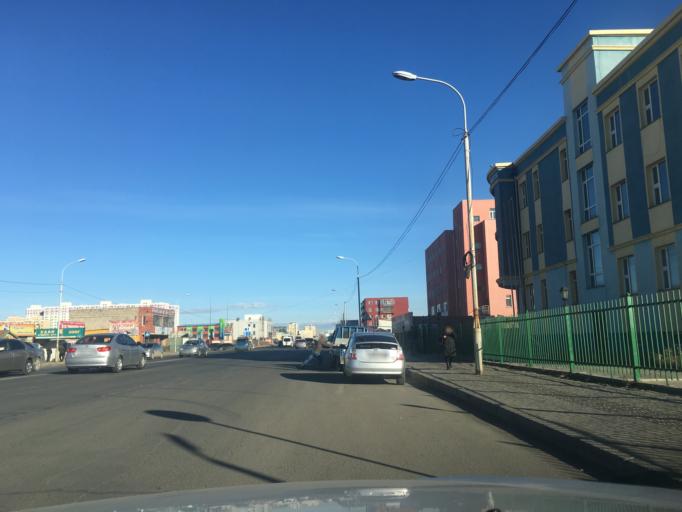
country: MN
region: Ulaanbaatar
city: Ulaanbaatar
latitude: 47.9080
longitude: 106.7947
